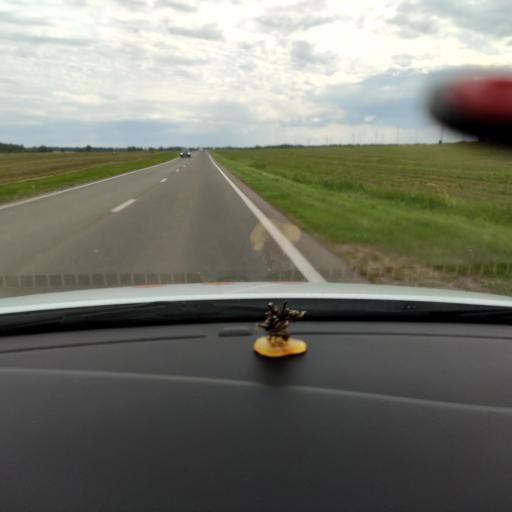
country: RU
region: Tatarstan
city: Stolbishchi
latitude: 55.4745
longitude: 49.2953
